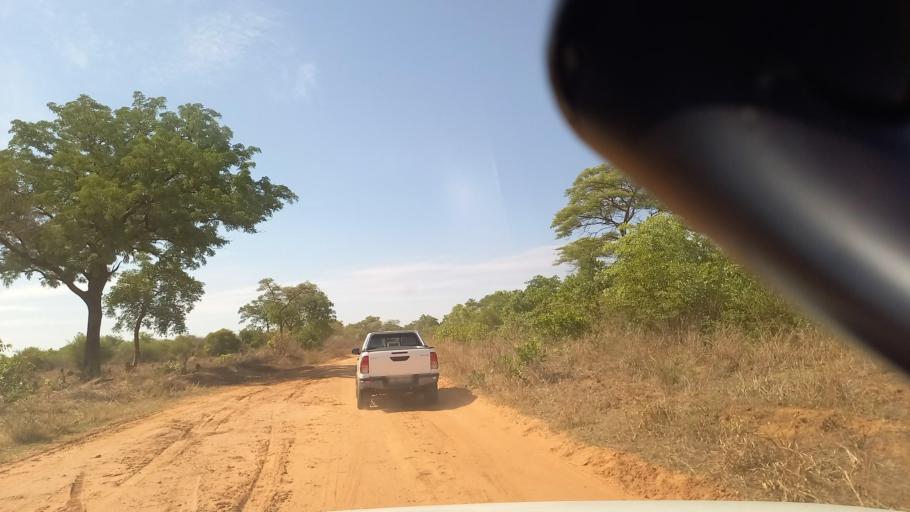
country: ZM
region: Southern
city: Mazabuka
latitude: -16.0346
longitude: 27.6175
